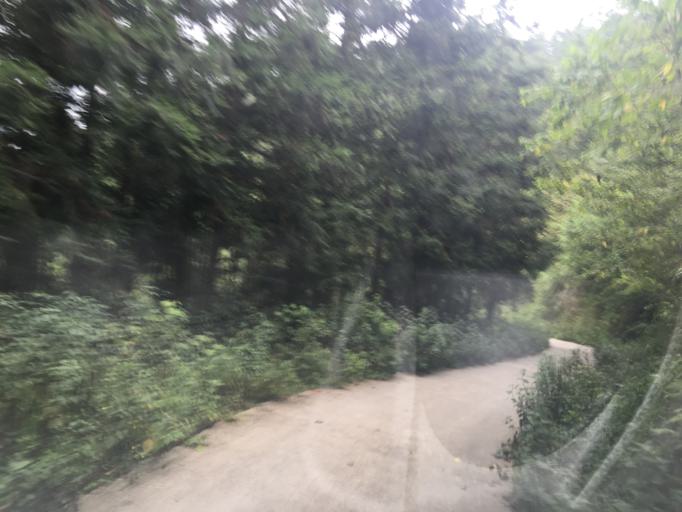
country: CN
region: Guangxi Zhuangzu Zizhiqu
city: Xinzhou
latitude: 25.1611
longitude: 105.6995
